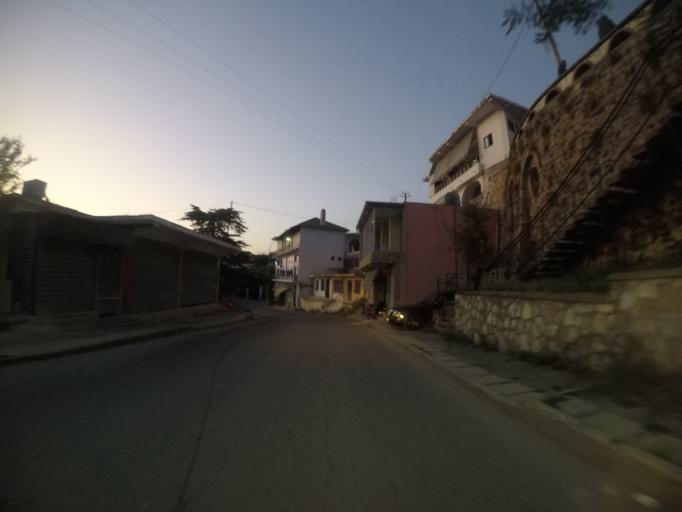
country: AL
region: Durres
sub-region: Rrethi i Krujes
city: Kruje
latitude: 41.5126
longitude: 19.7921
